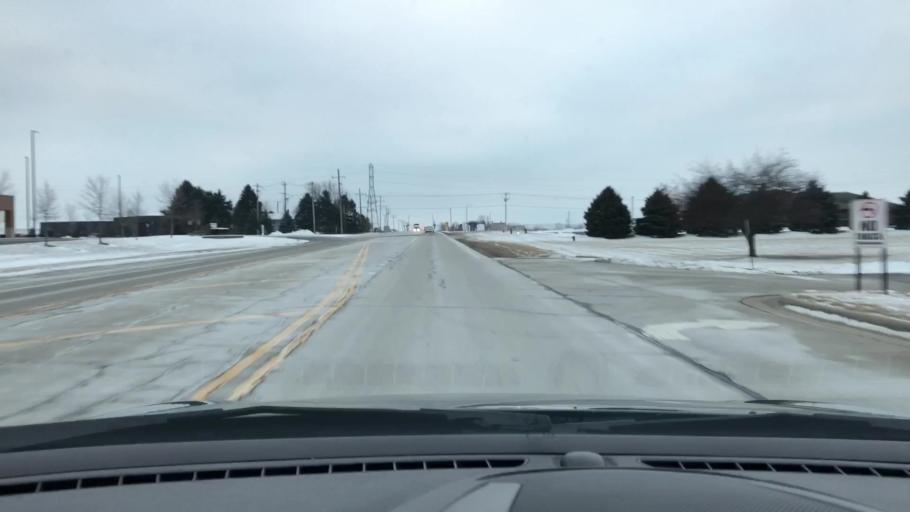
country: US
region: Illinois
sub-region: Will County
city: New Lenox
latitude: 41.4951
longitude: -88.0038
